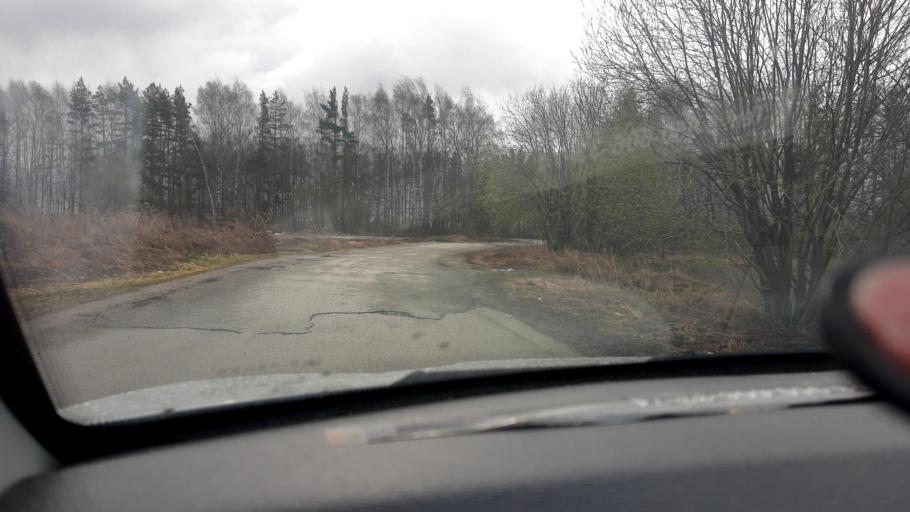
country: RU
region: Nizjnij Novgorod
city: Burevestnik
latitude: 56.1573
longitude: 43.7045
